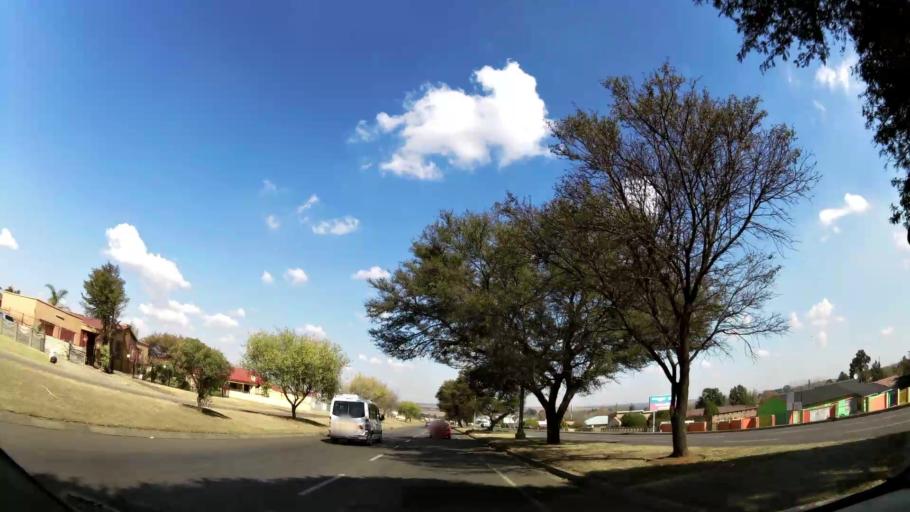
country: ZA
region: Mpumalanga
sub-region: Nkangala District Municipality
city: Witbank
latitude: -25.9102
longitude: 29.2362
